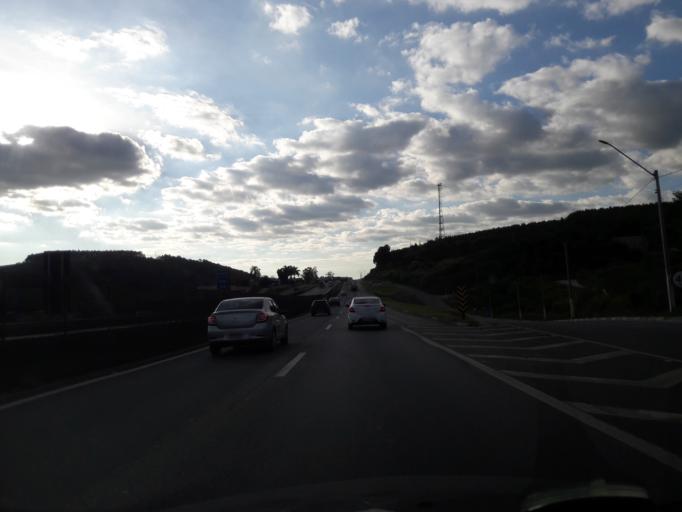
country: BR
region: Sao Paulo
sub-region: Atibaia
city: Atibaia
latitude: -23.0724
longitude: -46.5667
